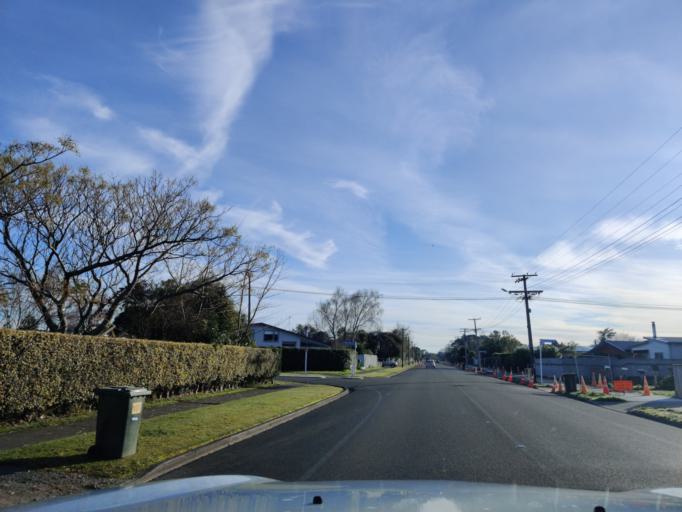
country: NZ
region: Manawatu-Wanganui
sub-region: Palmerston North City
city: Palmerston North
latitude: -40.2864
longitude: 175.7591
